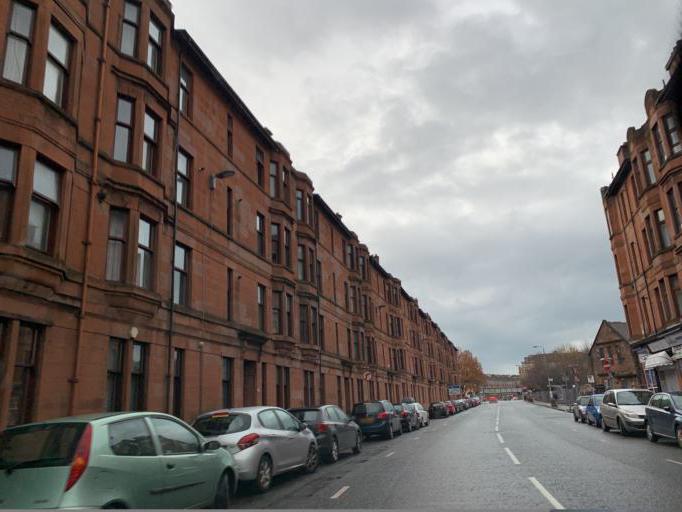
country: GB
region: Scotland
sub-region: East Renfrewshire
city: Clarkston
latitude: 55.8198
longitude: -4.2605
